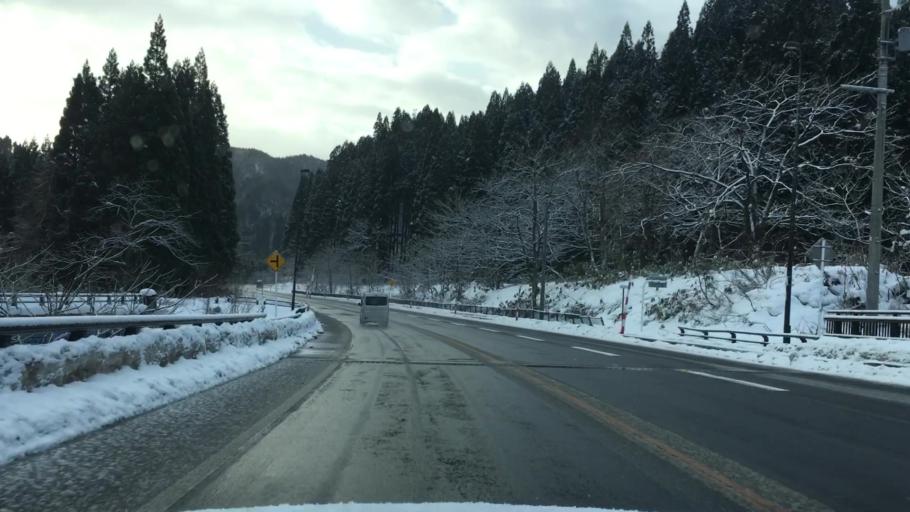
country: JP
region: Akita
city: Odate
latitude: 40.4143
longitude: 140.6113
